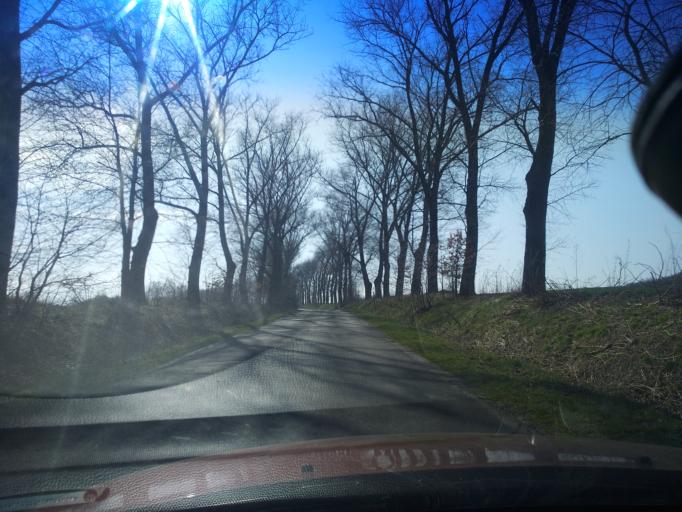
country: PL
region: Lower Silesian Voivodeship
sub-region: Powiat lubanski
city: Siekierczyn
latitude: 51.0595
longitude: 15.1566
